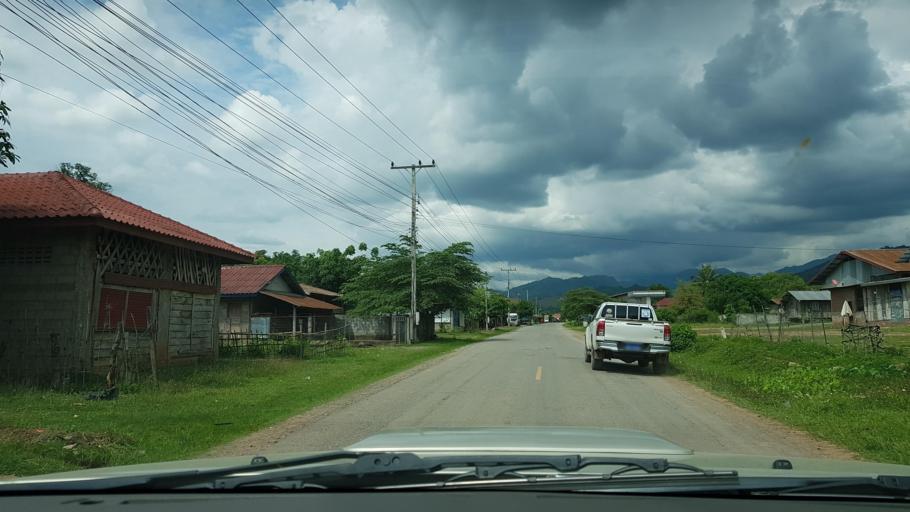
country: LA
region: Loungnamtha
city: Muang Nale
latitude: 20.2865
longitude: 101.6226
